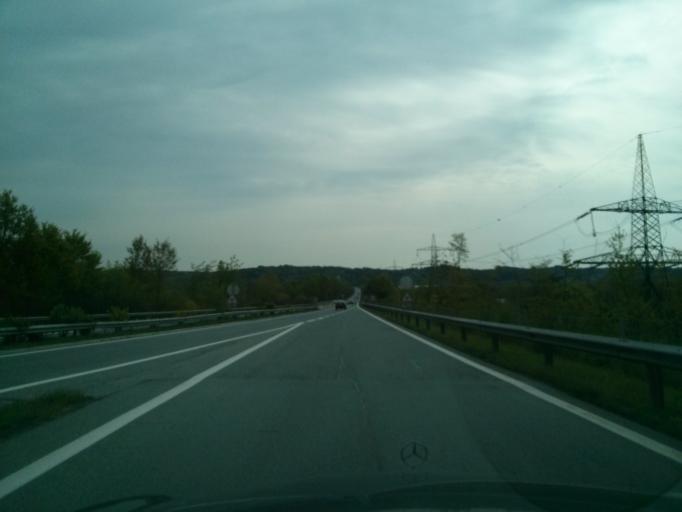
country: AT
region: Burgenland
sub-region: Politischer Bezirk Oberwart
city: Markt Allhau
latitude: 47.2803
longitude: 16.0666
